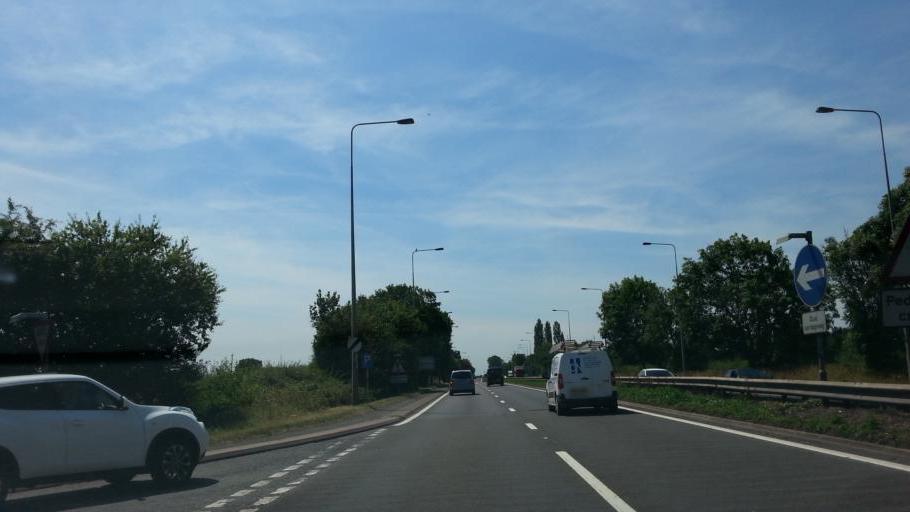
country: GB
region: England
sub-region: Staffordshire
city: Alrewas
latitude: 52.7138
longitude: -1.7626
